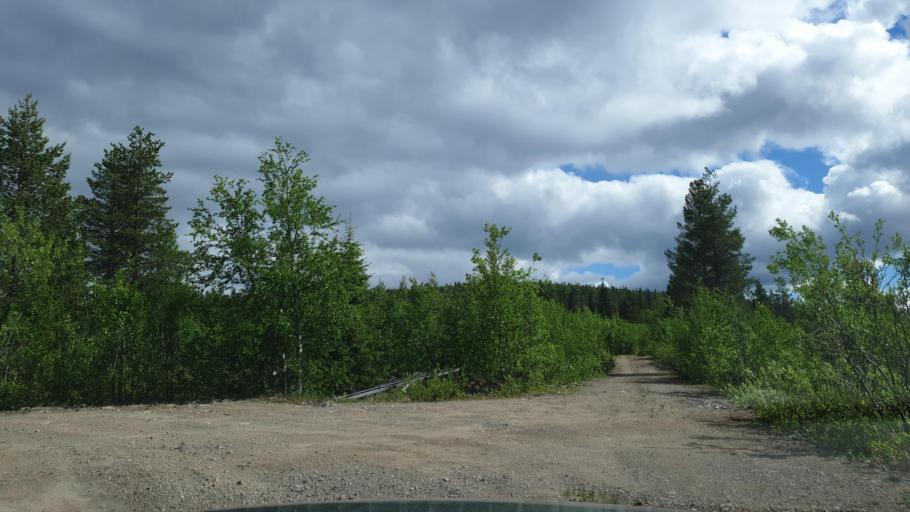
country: SE
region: Norrbotten
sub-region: Jokkmokks Kommun
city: Jokkmokk
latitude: 67.0301
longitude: 20.0027
